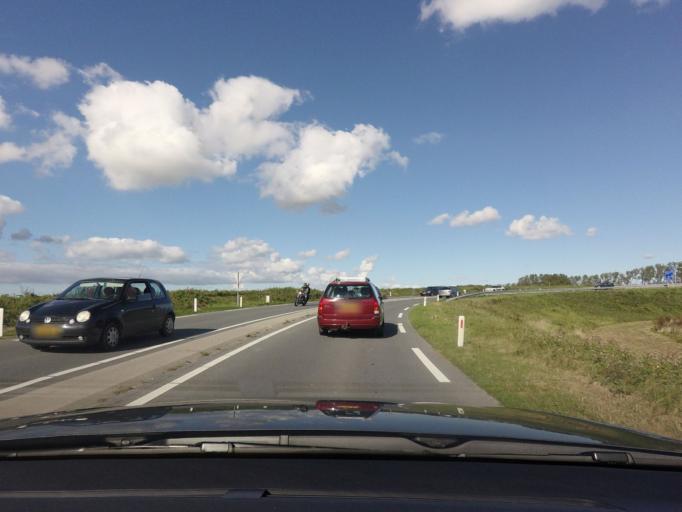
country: NL
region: North Holland
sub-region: Gemeente Schagen
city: Harenkarspel
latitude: 52.7081
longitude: 4.7120
